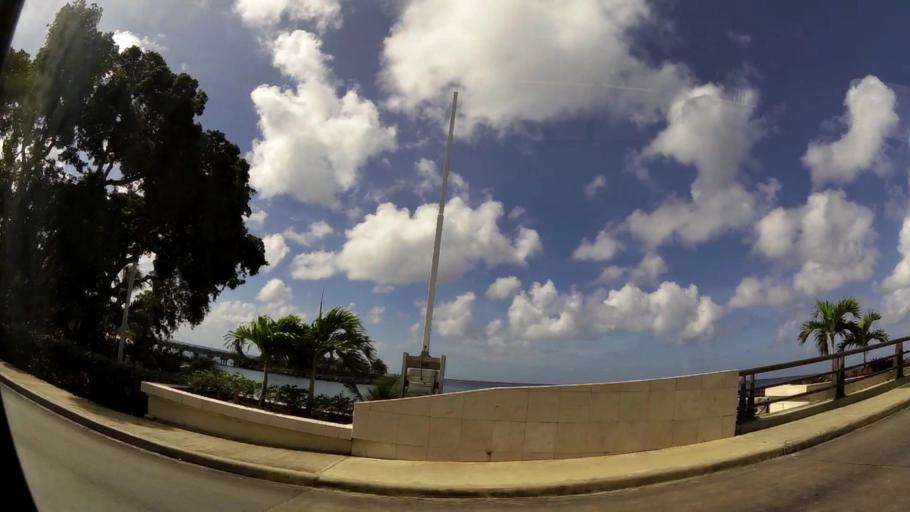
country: BB
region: Saint Peter
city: Speightstown
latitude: 13.2656
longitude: -59.6434
